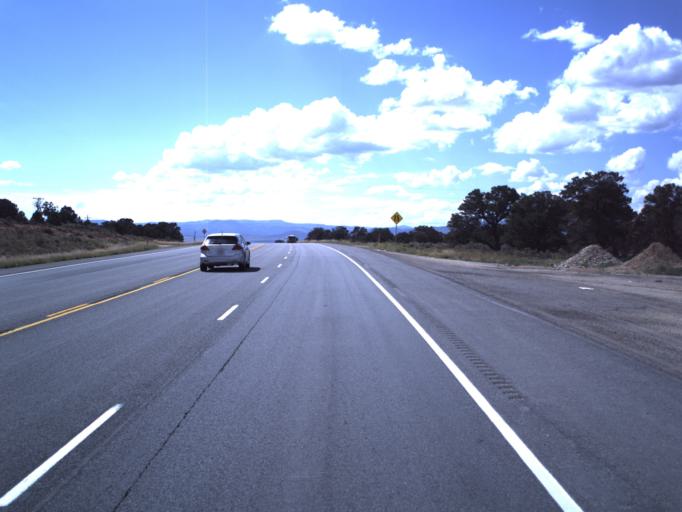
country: US
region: Utah
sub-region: Duchesne County
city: Duchesne
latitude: 40.1996
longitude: -110.6970
